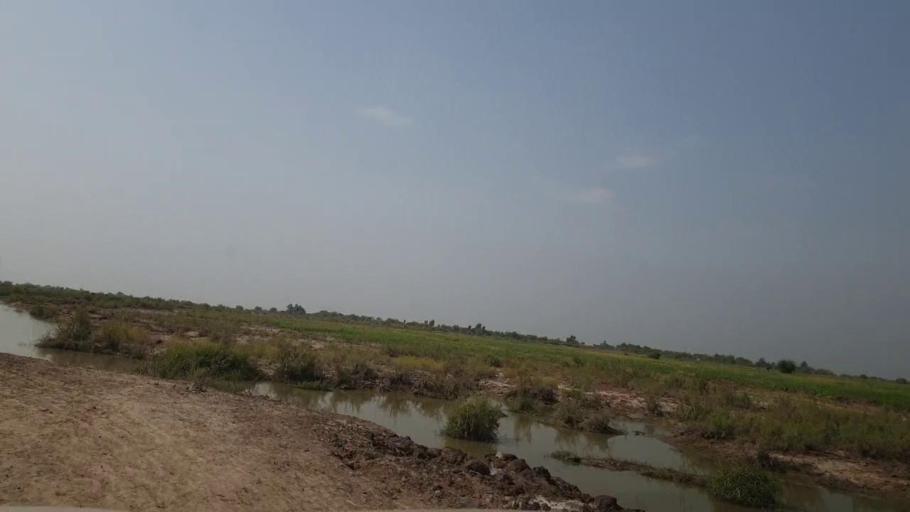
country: PK
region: Sindh
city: Dokri
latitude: 27.4116
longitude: 68.2019
